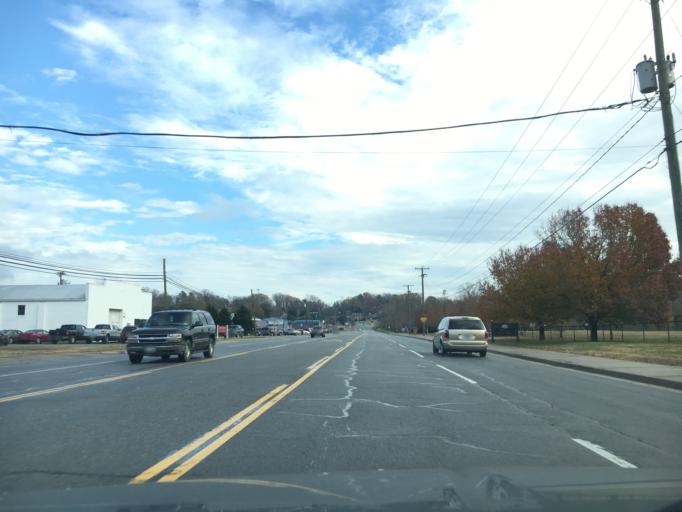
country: US
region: Virginia
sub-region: Prince Edward County
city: Farmville
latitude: 37.3040
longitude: -78.4108
